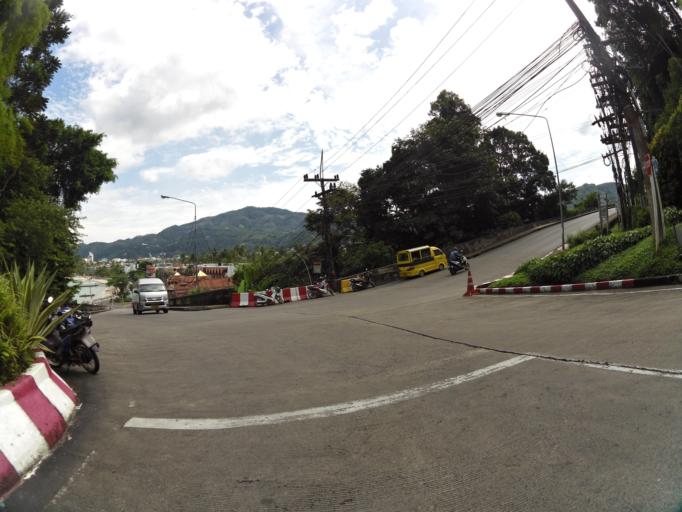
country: TH
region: Phuket
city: Patong
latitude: 7.8851
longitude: 98.2865
